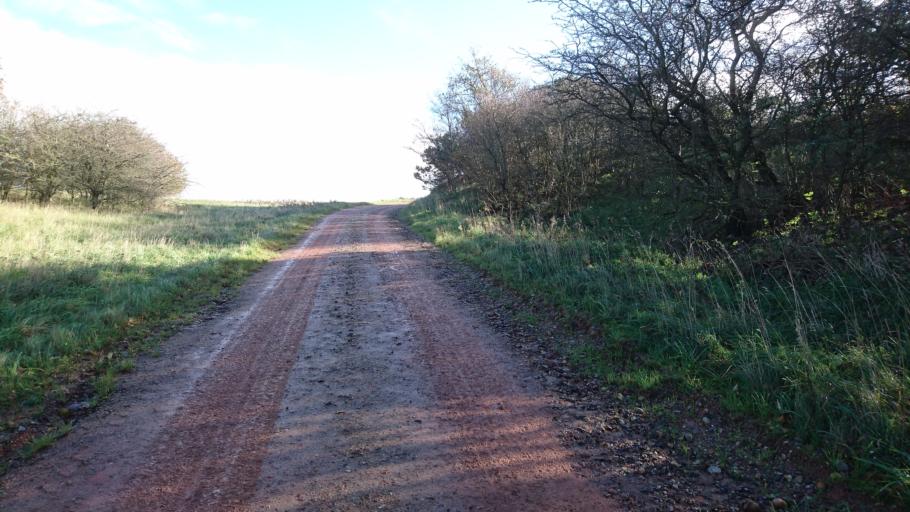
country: DK
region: North Denmark
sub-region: Morso Kommune
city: Nykobing Mors
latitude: 56.8331
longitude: 9.0022
